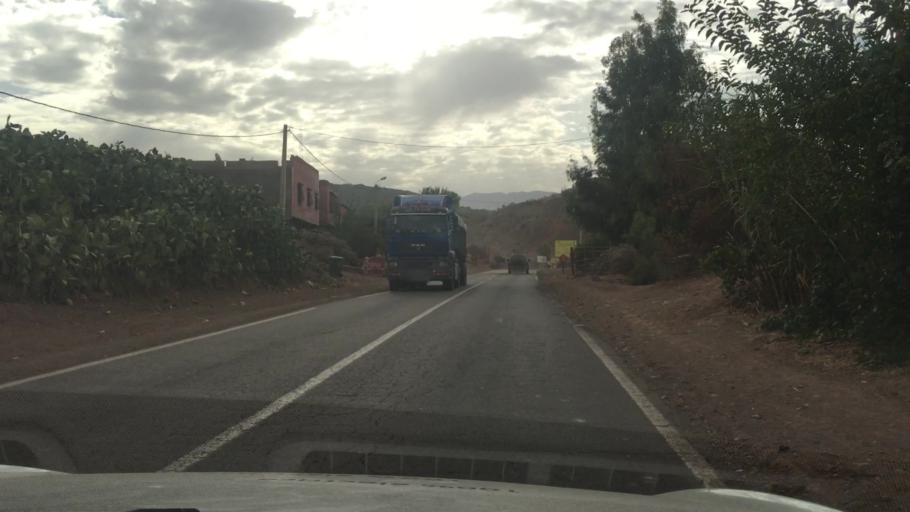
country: MA
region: Marrakech-Tensift-Al Haouz
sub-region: Al-Haouz
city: Touama
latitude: 31.5474
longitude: -7.5744
